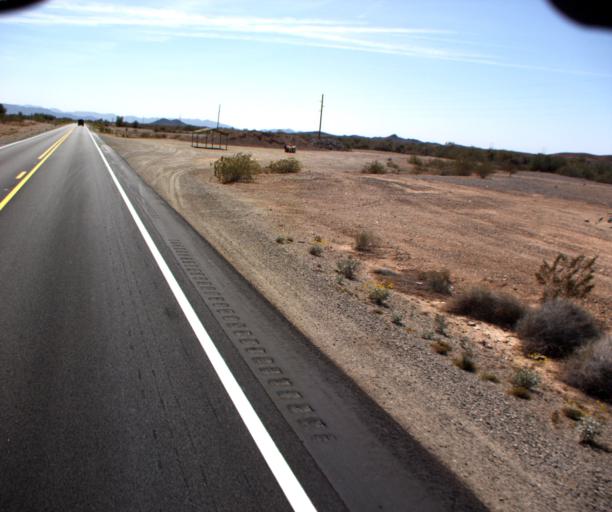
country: US
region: Arizona
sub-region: Yuma County
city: Wellton
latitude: 32.9799
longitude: -114.2893
